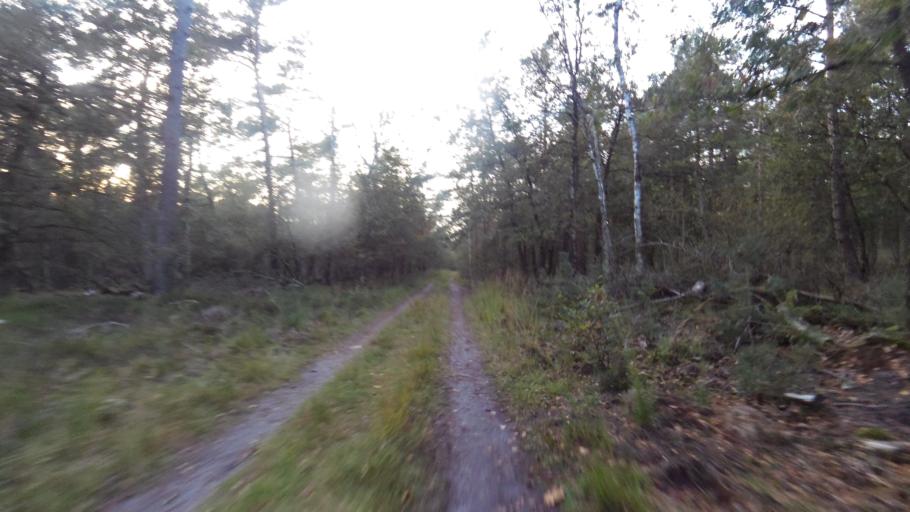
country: NL
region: Gelderland
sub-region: Gemeente Nunspeet
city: Nunspeet
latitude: 52.3280
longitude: 5.7960
